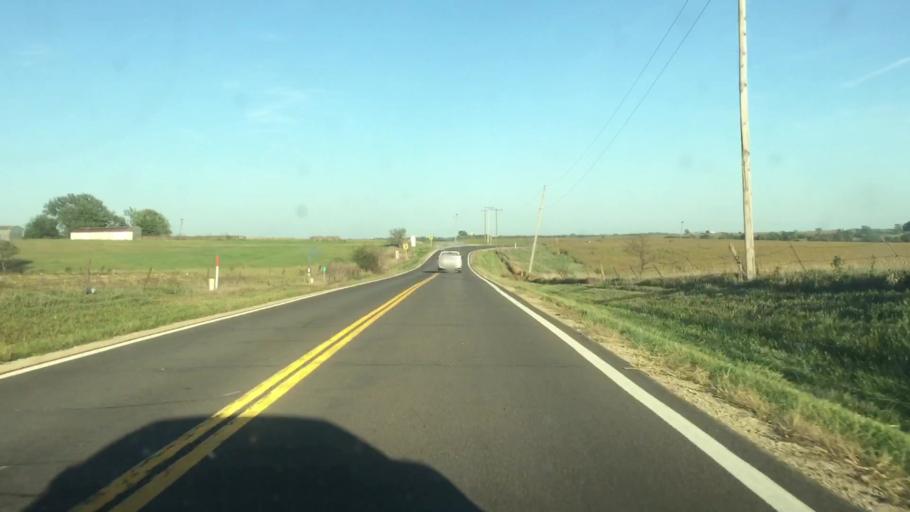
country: US
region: Kansas
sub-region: Brown County
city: Horton
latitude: 39.5511
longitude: -95.4058
